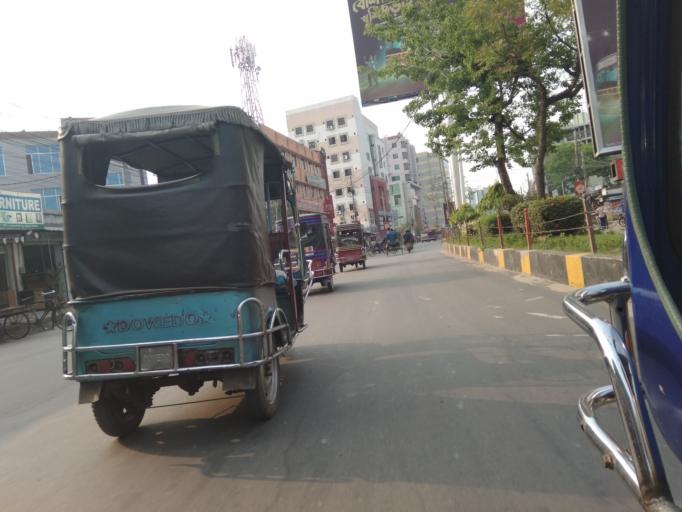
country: BD
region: Khulna
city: Khulna
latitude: 22.8152
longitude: 89.5546
